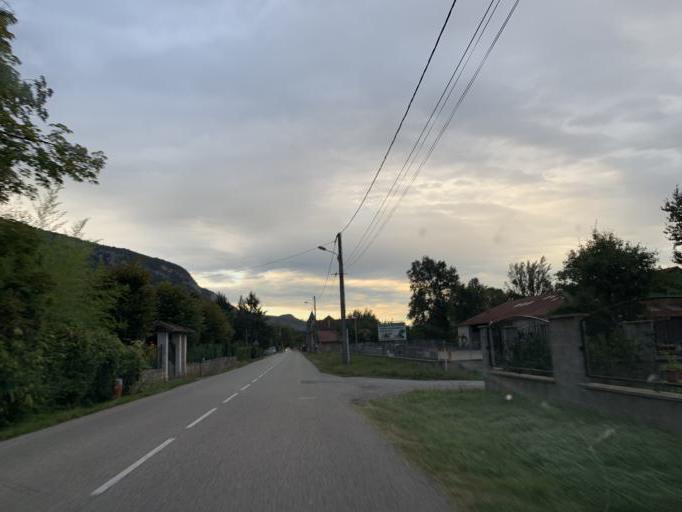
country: FR
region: Rhone-Alpes
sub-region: Departement de l'Isere
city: Les Avenieres
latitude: 45.6970
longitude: 5.5854
